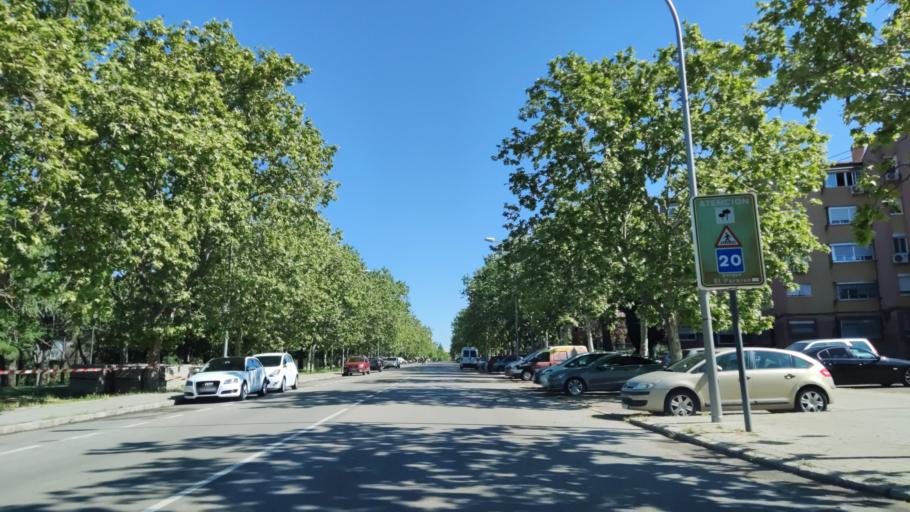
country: ES
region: Madrid
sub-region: Provincia de Madrid
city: San Blas
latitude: 40.4291
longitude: -3.6203
